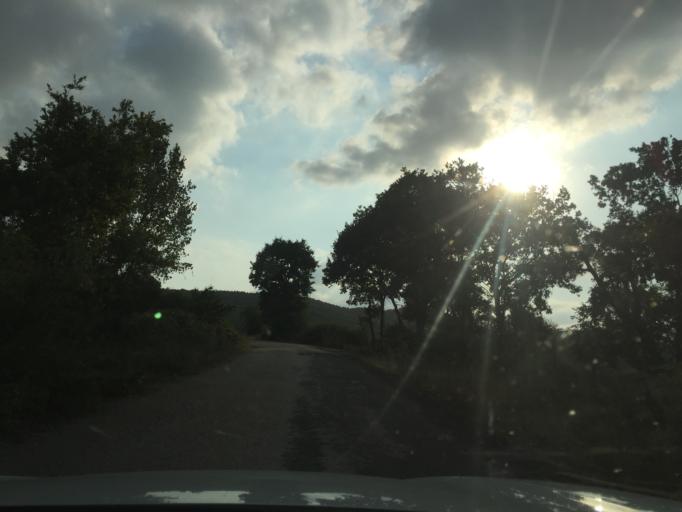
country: TR
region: Balikesir
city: Gonen
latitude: 40.0334
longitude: 27.5670
